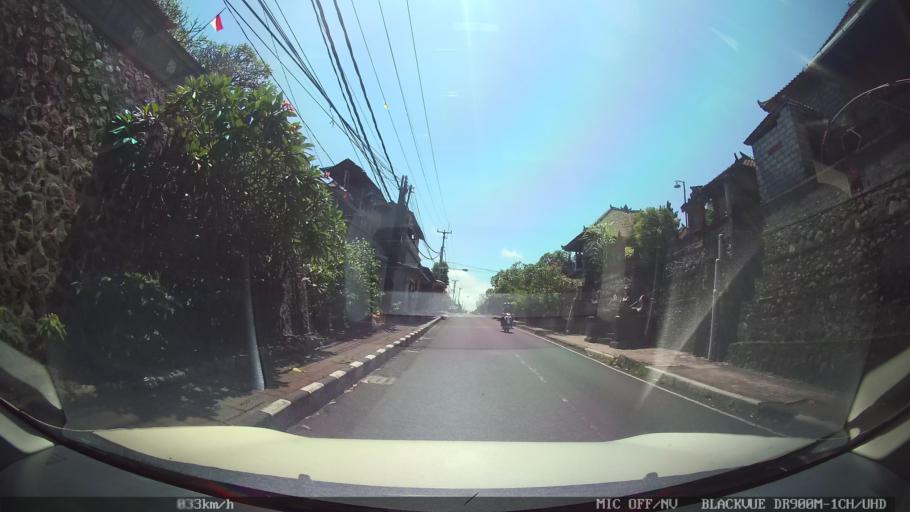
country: ID
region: Bali
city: Klungkung
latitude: -8.5771
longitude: 115.3507
